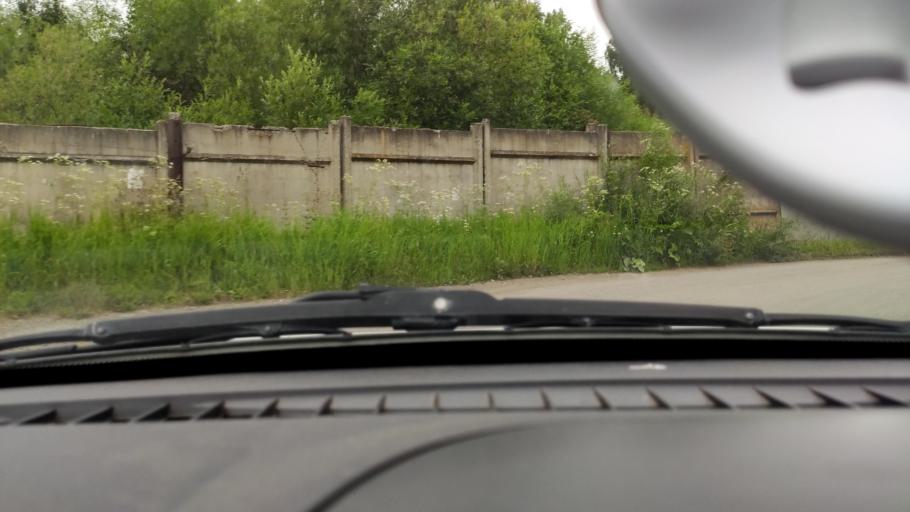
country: RU
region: Perm
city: Ferma
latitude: 57.8879
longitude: 56.2972
